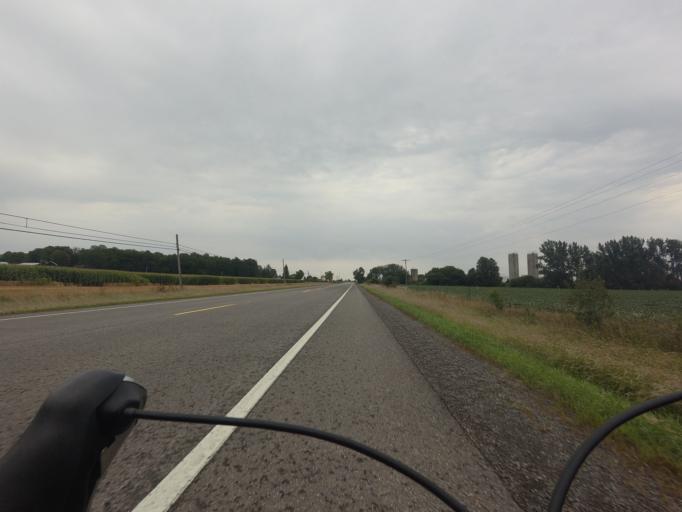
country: CA
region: Ontario
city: Bells Corners
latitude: 45.1508
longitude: -75.7404
